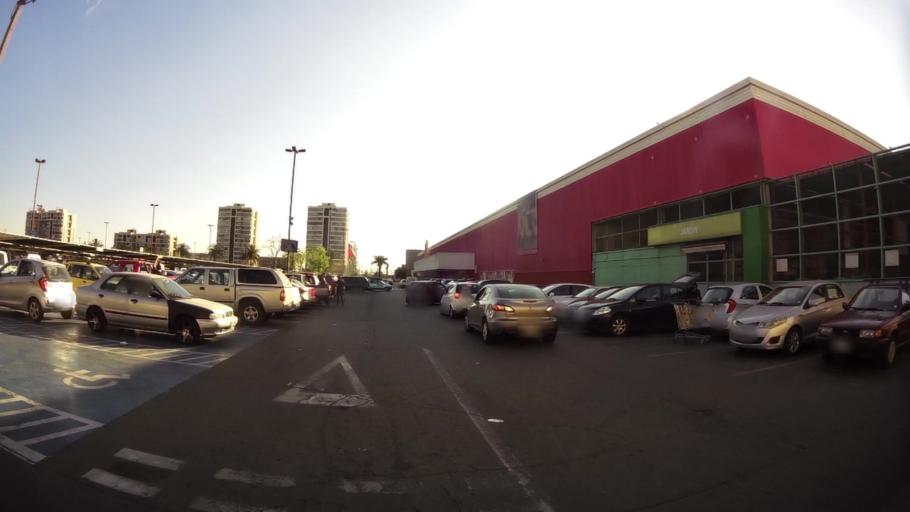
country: CL
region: Santiago Metropolitan
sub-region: Provincia de Santiago
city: Lo Prado
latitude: -33.4800
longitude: -70.7526
